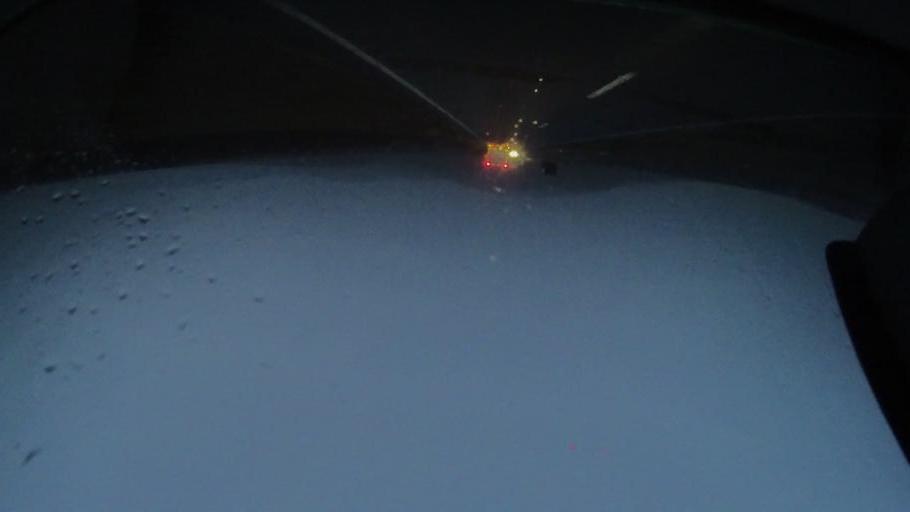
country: RO
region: Harghita
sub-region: Comuna Ditrau
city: Ditrau
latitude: 46.8339
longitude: 25.4914
